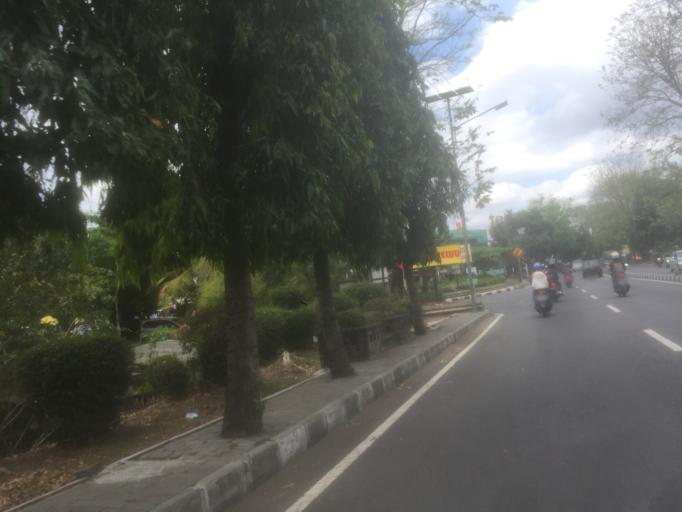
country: ID
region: Daerah Istimewa Yogyakarta
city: Melati
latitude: -7.7281
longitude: 110.3632
